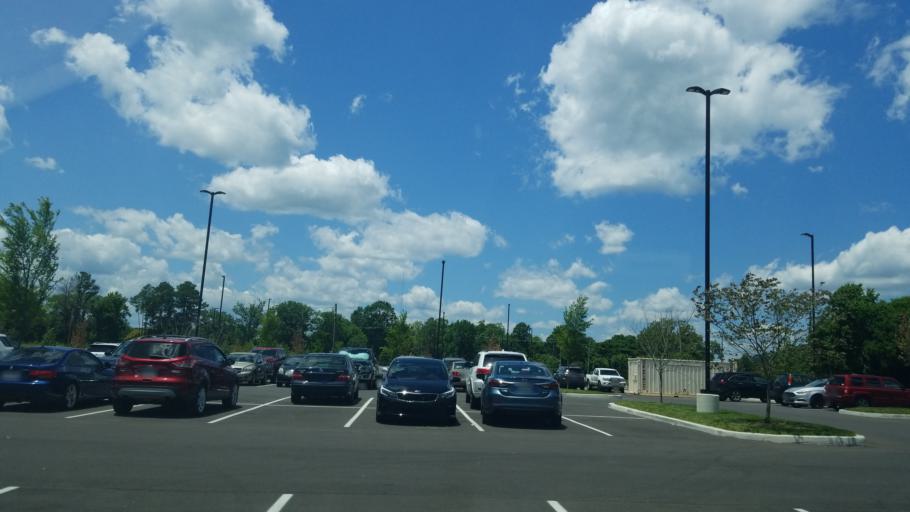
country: US
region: Tennessee
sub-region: Williamson County
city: Brentwood
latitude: 36.0338
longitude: -86.8142
